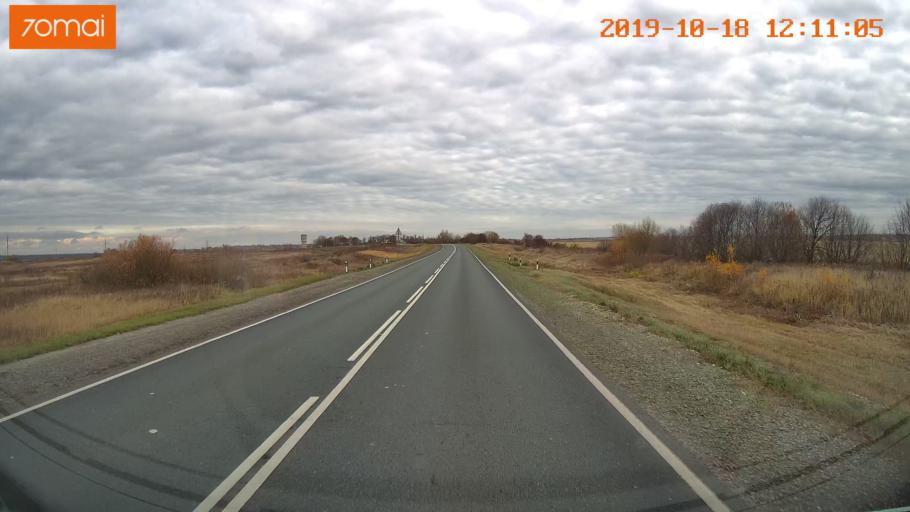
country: RU
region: Rjazan
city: Zakharovo
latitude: 54.3980
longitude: 39.3448
